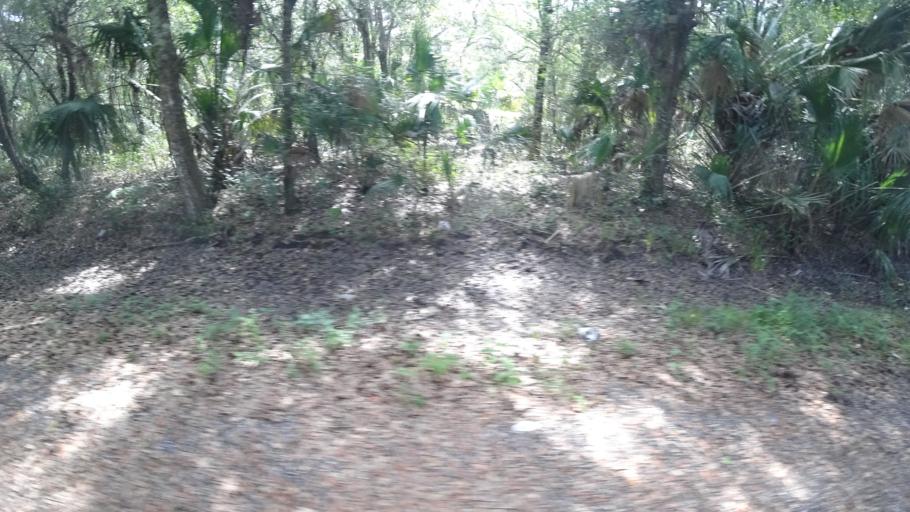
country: US
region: Florida
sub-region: Manatee County
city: Ellenton
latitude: 27.4896
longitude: -82.4786
